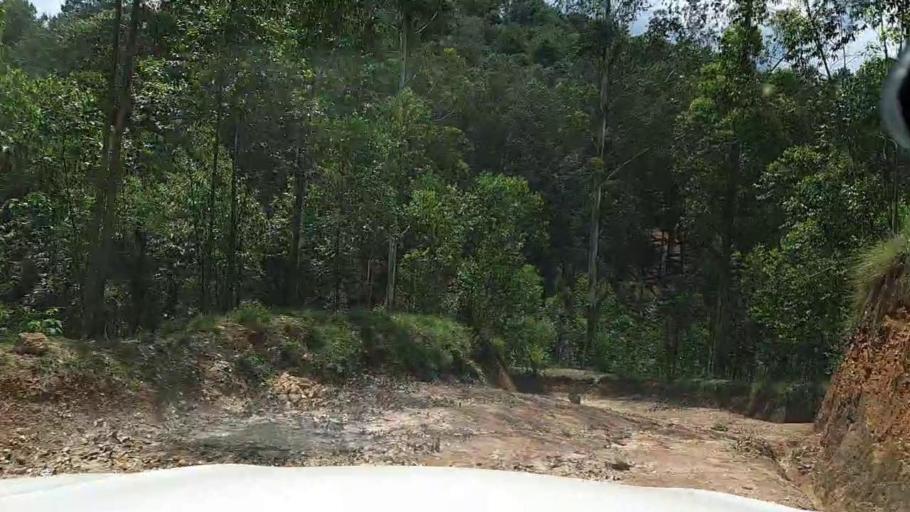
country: RW
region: Southern Province
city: Nzega
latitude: -2.6453
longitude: 29.4766
